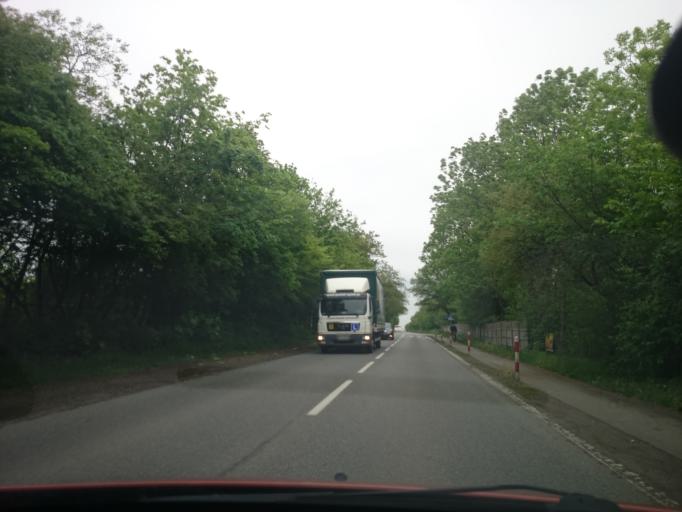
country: PL
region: Opole Voivodeship
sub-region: Powiat opolski
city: Opole
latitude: 50.6840
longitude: 17.9258
